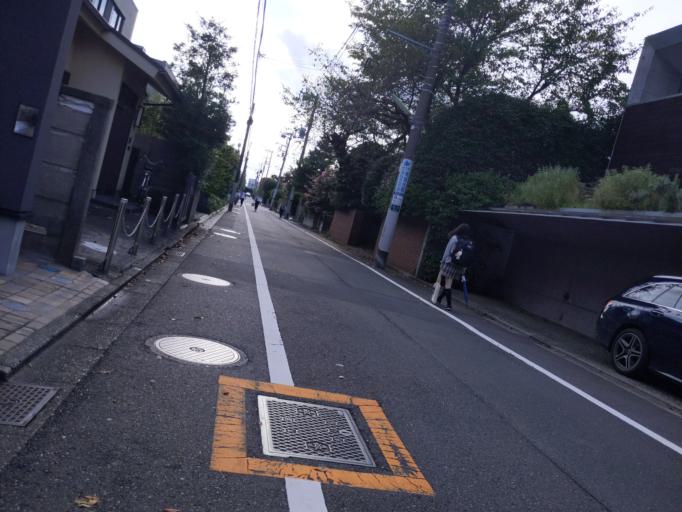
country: JP
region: Tokyo
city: Chofugaoka
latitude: 35.6397
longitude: 139.5956
